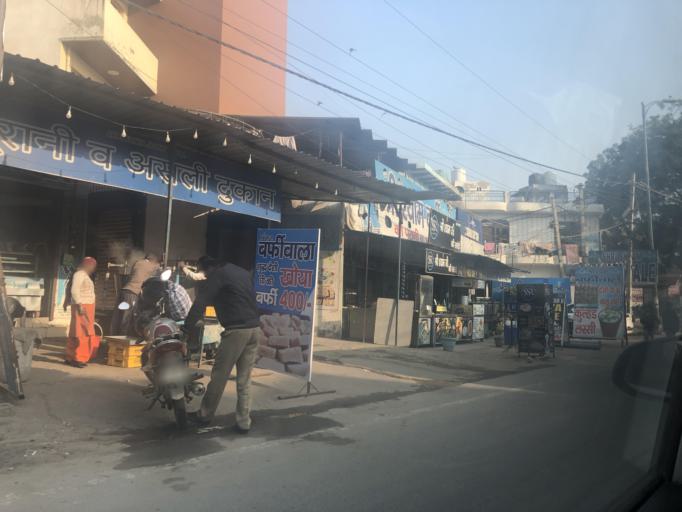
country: IN
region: Haryana
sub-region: Gurgaon
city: Gurgaon
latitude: 28.5595
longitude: 77.0033
